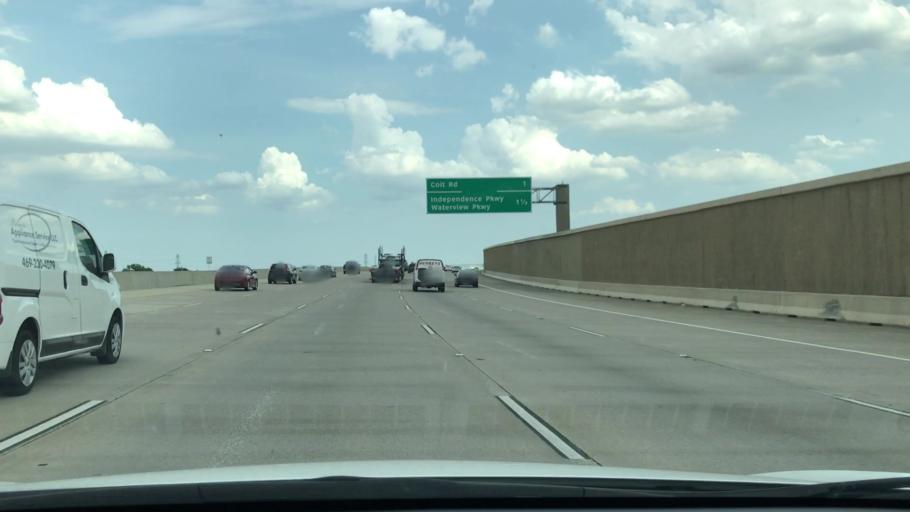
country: US
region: Texas
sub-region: Dallas County
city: Addison
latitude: 33.0099
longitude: -96.7869
